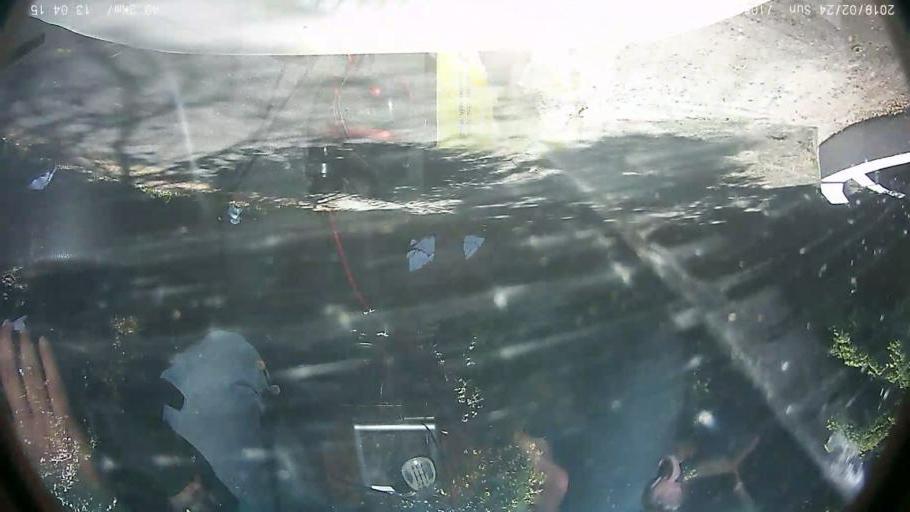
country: IN
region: Tamil Nadu
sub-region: Nilgiri
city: Wellington
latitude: 11.3367
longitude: 76.8278
